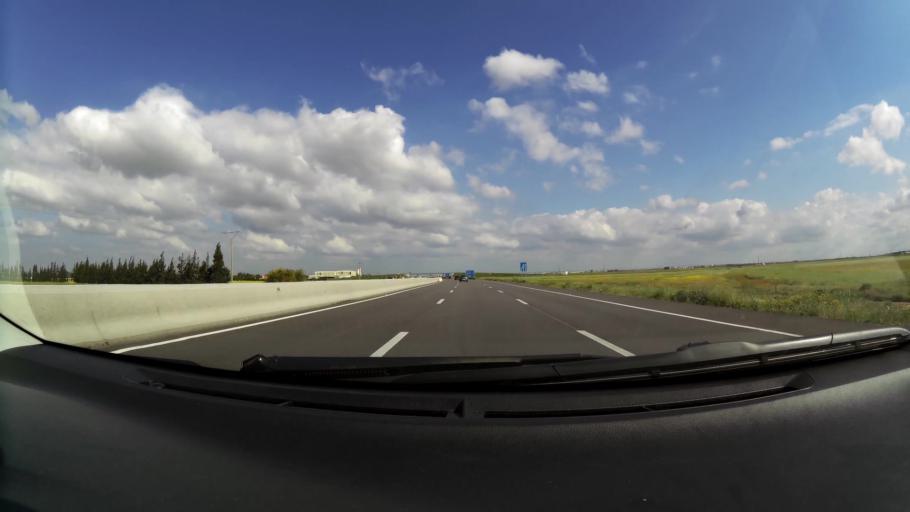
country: MA
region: Chaouia-Ouardigha
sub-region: Settat Province
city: Berrechid
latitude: 33.3153
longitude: -7.5998
